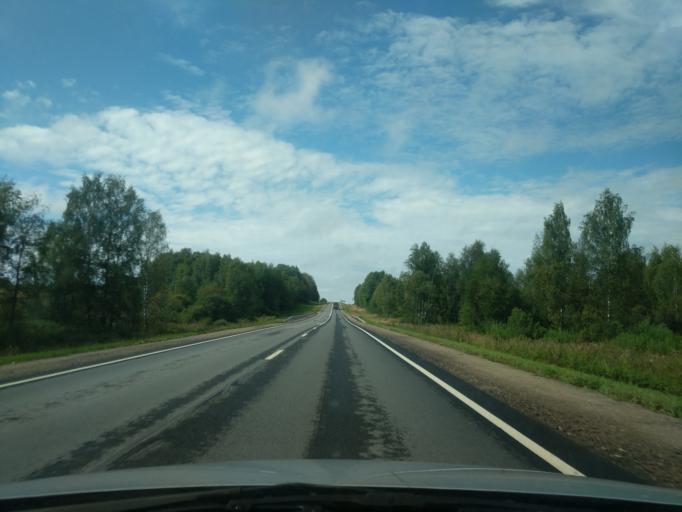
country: RU
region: Kostroma
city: Sudislavl'
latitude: 57.8390
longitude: 41.8526
